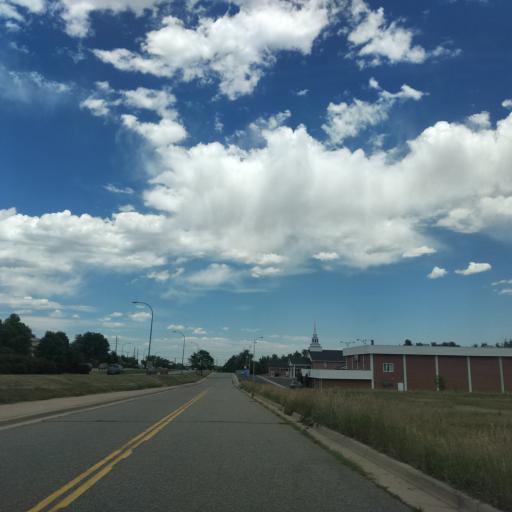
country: US
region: Colorado
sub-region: Jefferson County
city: Lakewood
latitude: 39.7066
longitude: -105.1093
